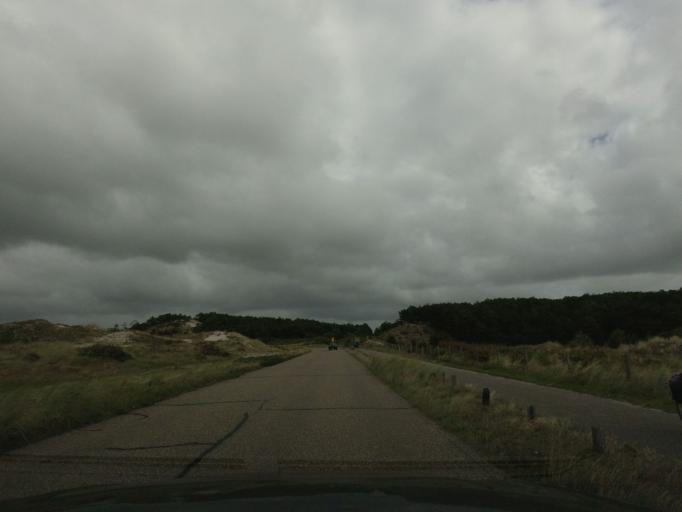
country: NL
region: North Holland
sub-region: Gemeente Bergen
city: Egmond aan Zee
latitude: 52.7148
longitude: 4.6455
